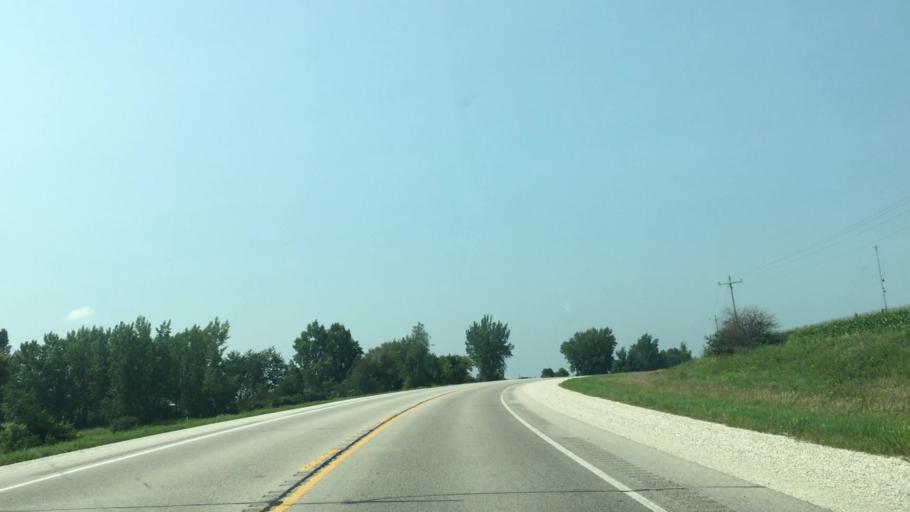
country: US
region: Iowa
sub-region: Winneshiek County
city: Decorah
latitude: 43.1944
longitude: -91.8722
